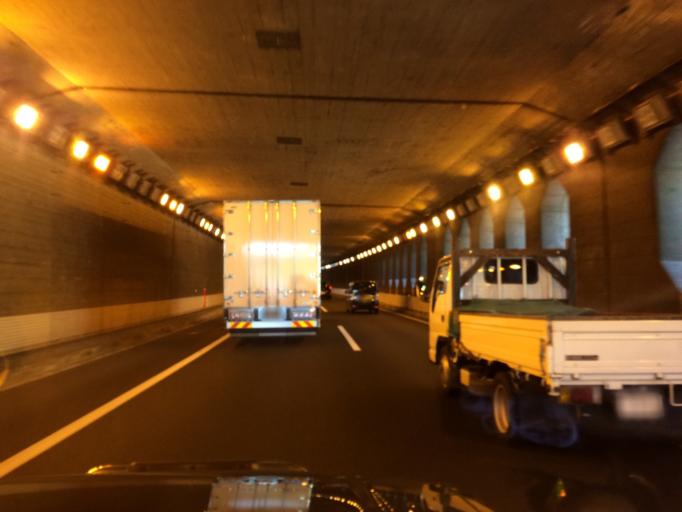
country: JP
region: Osaka
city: Izumi
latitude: 34.4920
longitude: 135.4681
